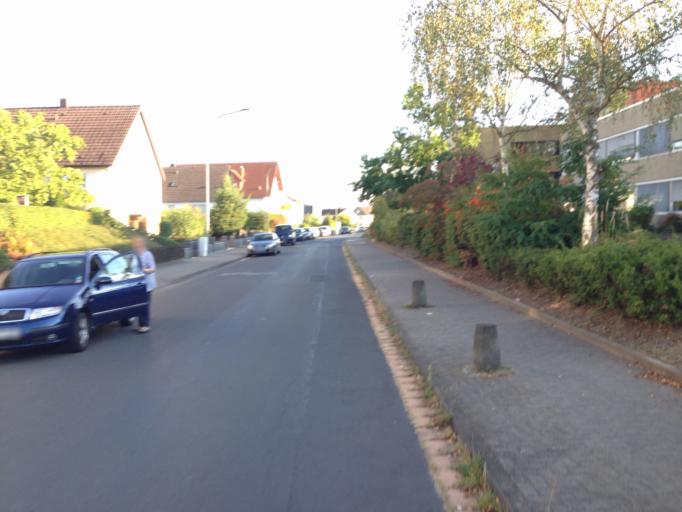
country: DE
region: Hesse
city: Lollar
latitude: 50.6122
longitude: 8.7102
